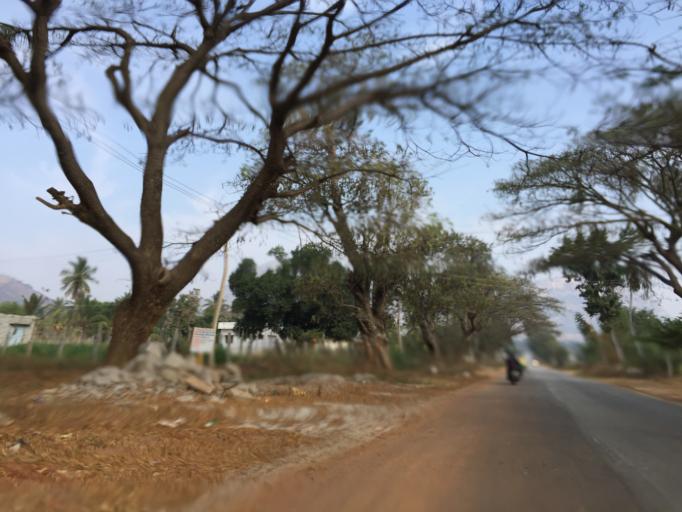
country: IN
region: Karnataka
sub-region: Bangalore Rural
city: Devanhalli
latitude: 13.3312
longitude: 77.6909
